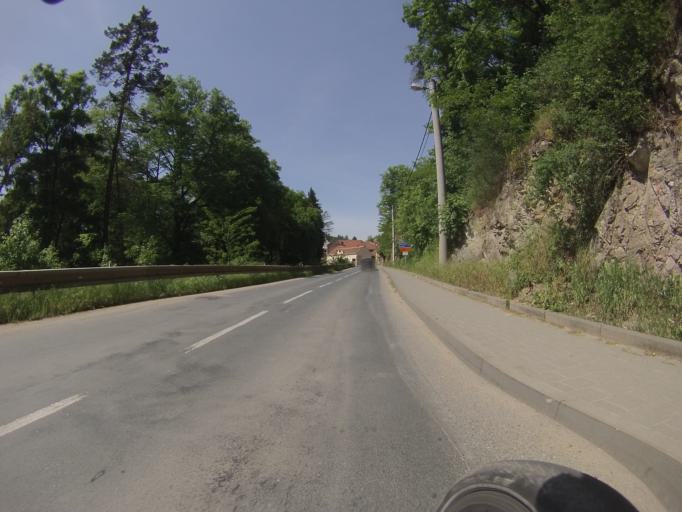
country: CZ
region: South Moravian
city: Bilovice nad Svitavou
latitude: 49.2469
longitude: 16.6745
